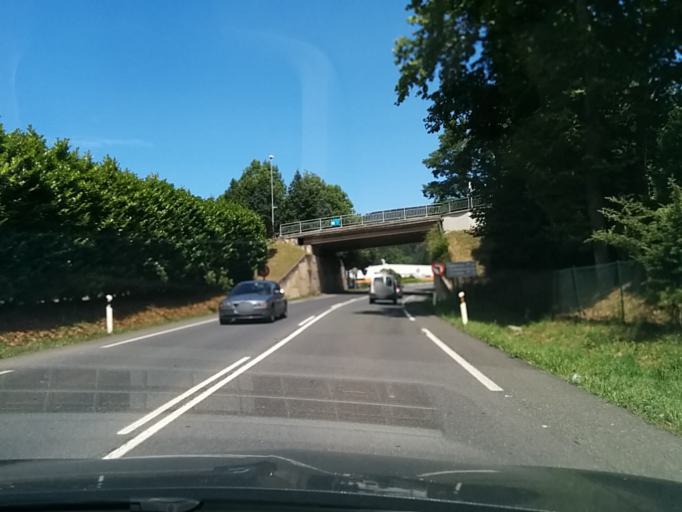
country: ES
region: Basque Country
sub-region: Provincia de Guipuzcoa
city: Usurbil
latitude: 43.2709
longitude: -2.0536
